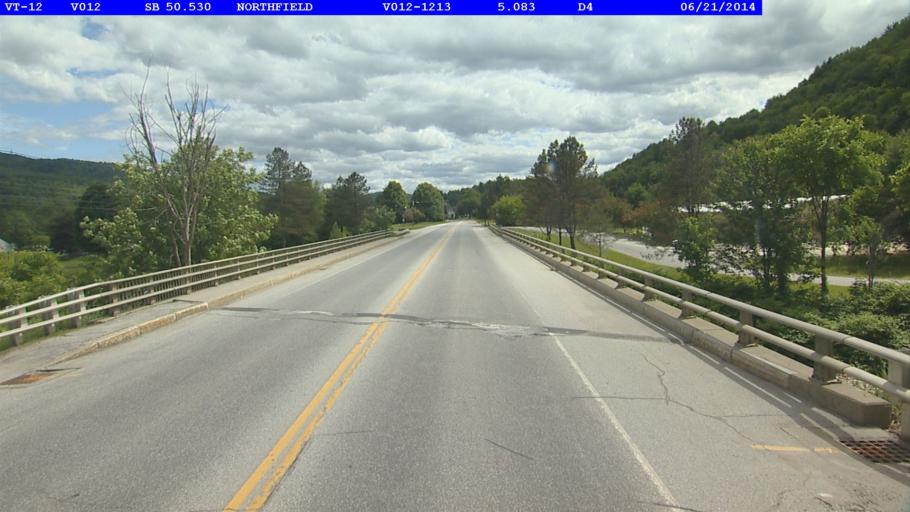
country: US
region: Vermont
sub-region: Washington County
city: Northfield
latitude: 44.1616
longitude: -72.6565
